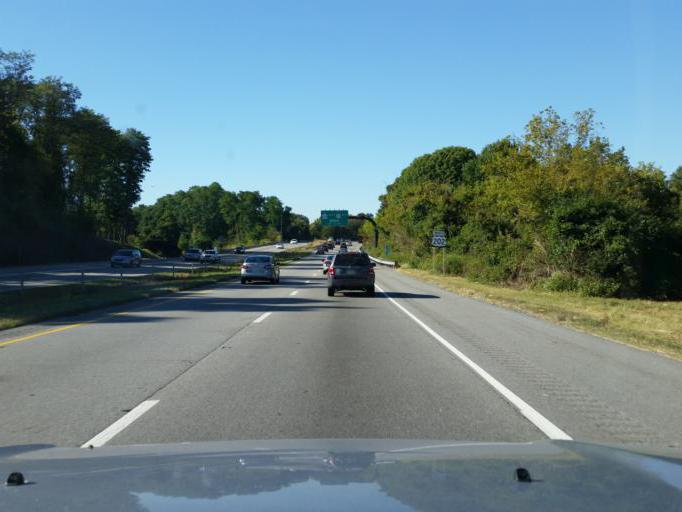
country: US
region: Pennsylvania
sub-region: Chester County
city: West Chester
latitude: 39.9788
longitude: -75.5869
